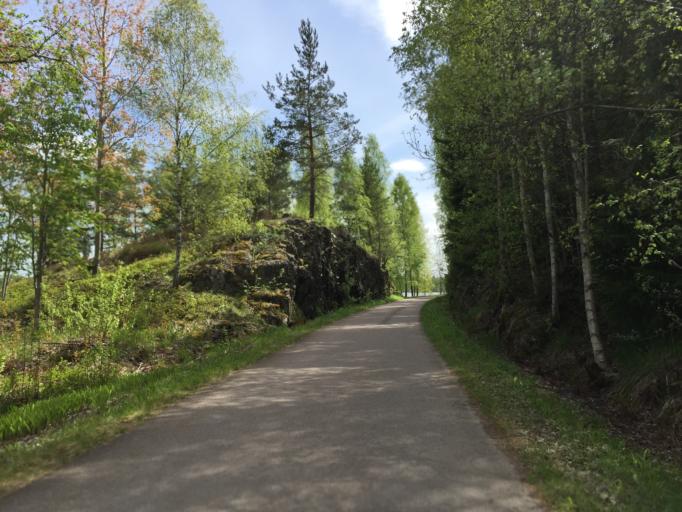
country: SE
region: Dalarna
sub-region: Ludvika Kommun
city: Ludvika
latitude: 60.1443
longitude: 15.1584
